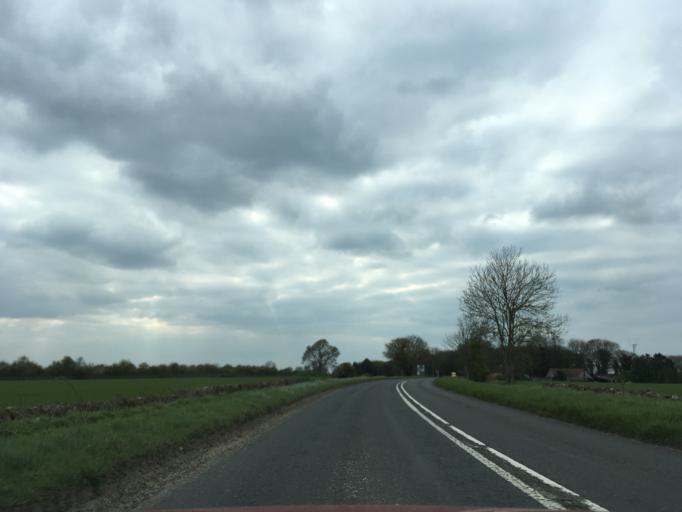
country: GB
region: England
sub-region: Oxfordshire
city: Carterton
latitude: 51.7894
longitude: -1.5765
